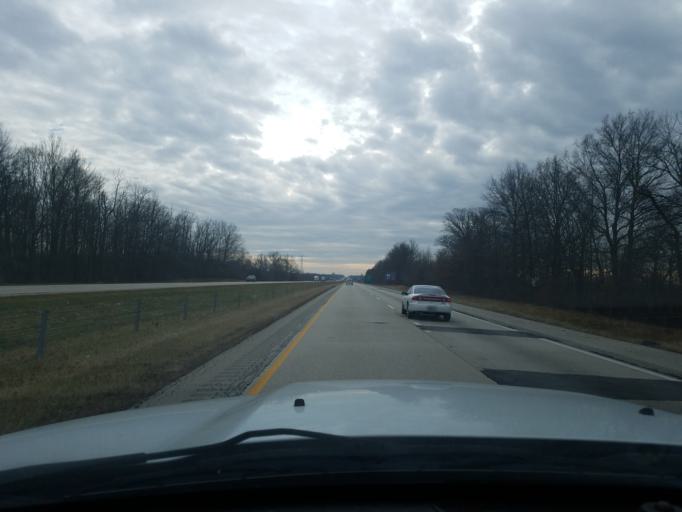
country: US
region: Indiana
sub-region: Grant County
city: Marion
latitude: 40.5779
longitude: -85.5516
